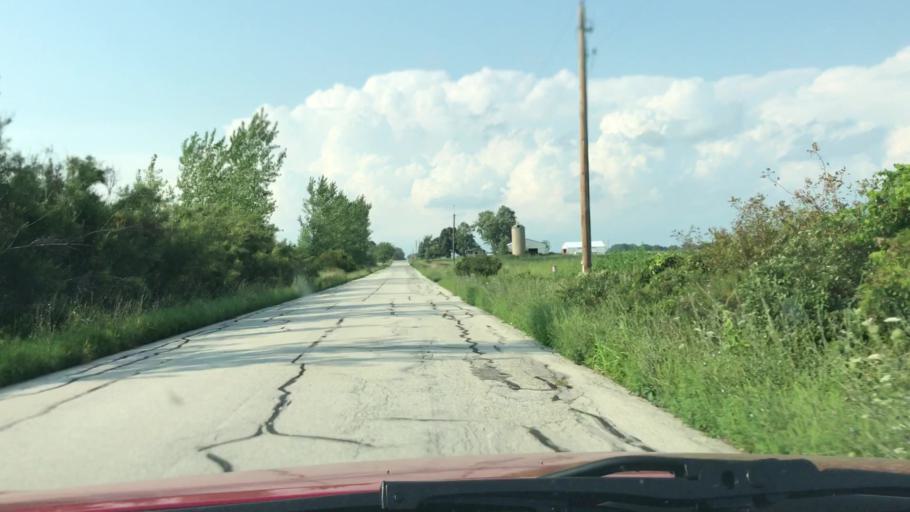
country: US
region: Wisconsin
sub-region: Brown County
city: Oneida
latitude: 44.4403
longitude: -88.1704
